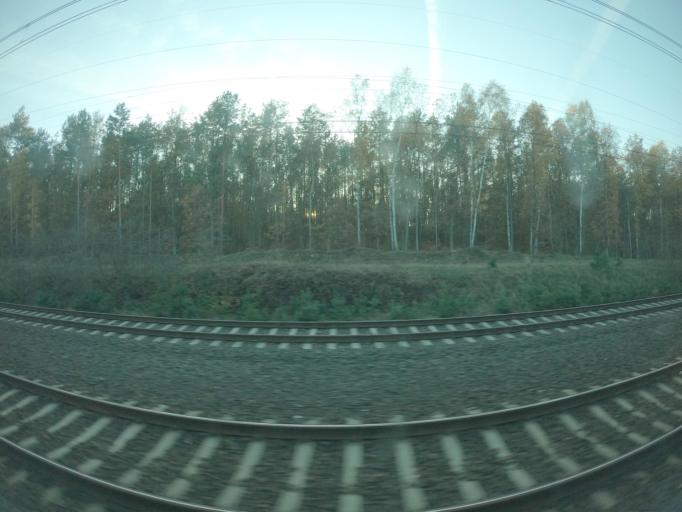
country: PL
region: Lubusz
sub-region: Powiat slubicki
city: Rzepin
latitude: 52.3170
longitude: 14.8550
